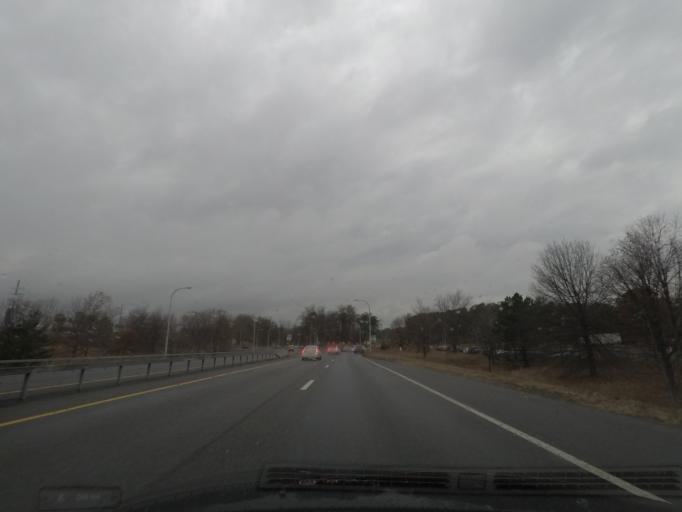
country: US
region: New York
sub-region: Albany County
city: Roessleville
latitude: 42.6942
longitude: -73.8275
